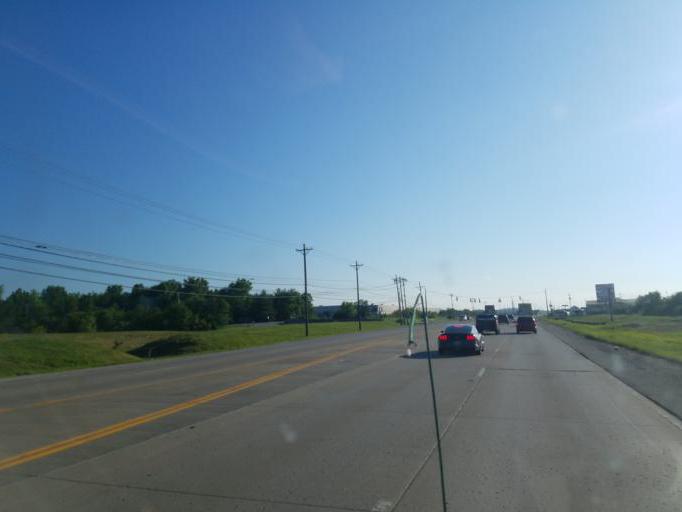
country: US
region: Kentucky
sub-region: Jefferson County
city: Heritage Creek
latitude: 38.1332
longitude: -85.7248
